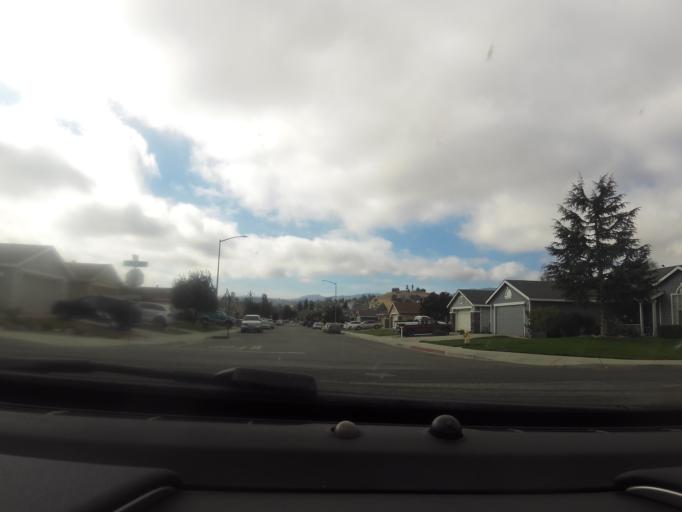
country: US
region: California
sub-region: San Benito County
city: Ridgemark
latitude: 36.8263
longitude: -121.3773
